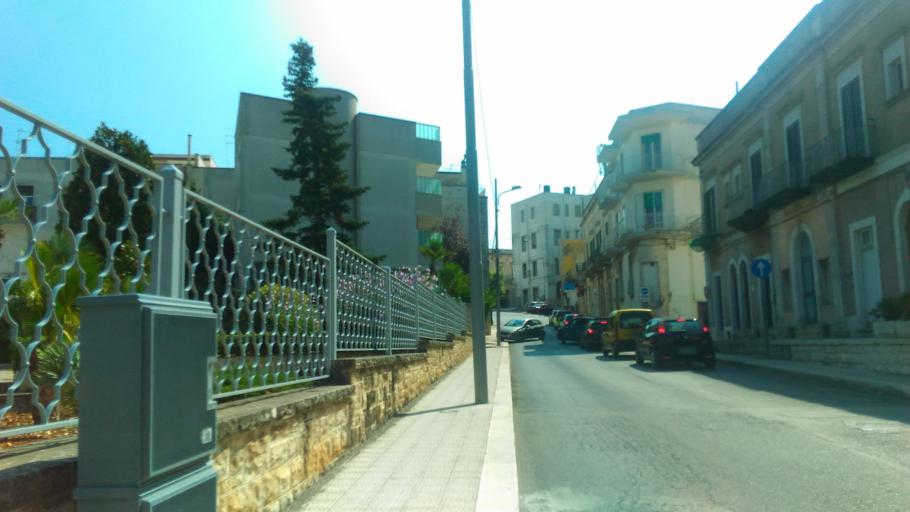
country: IT
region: Apulia
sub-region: Provincia di Bari
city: Locorotondo
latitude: 40.7549
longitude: 17.3251
